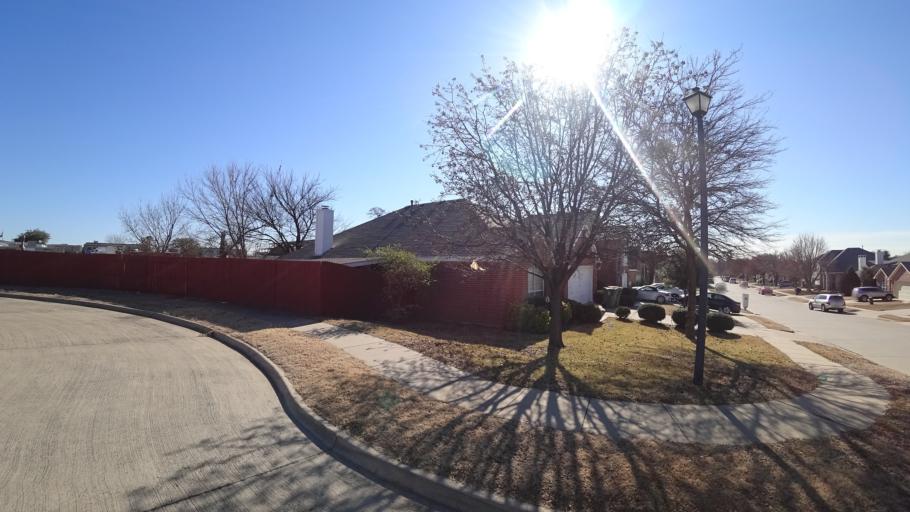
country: US
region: Texas
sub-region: Denton County
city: Lewisville
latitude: 33.0272
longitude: -97.0270
